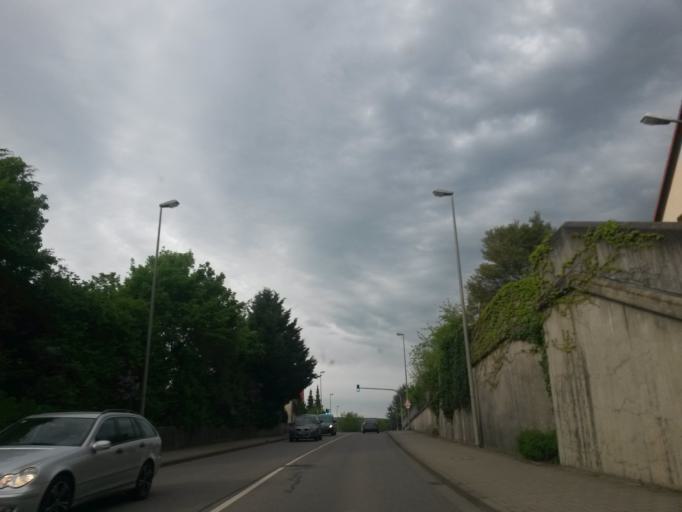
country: DE
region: Bavaria
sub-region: Upper Franconia
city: Hirschaid
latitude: 49.8188
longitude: 10.9931
